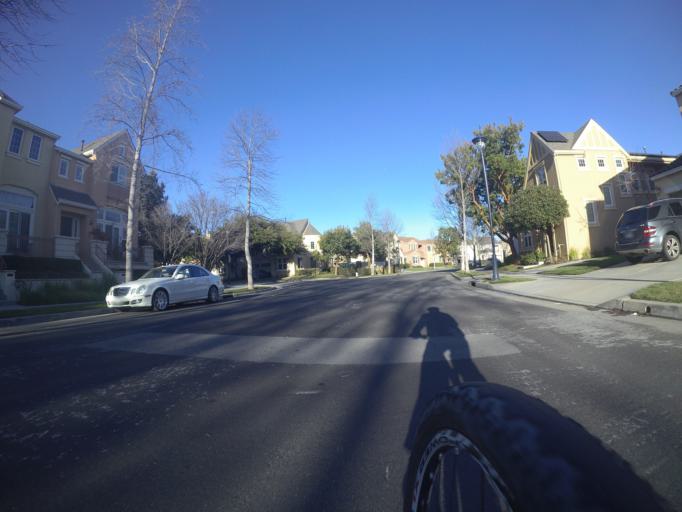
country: US
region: California
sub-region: Santa Clara County
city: Santa Clara
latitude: 37.3997
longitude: -121.9524
